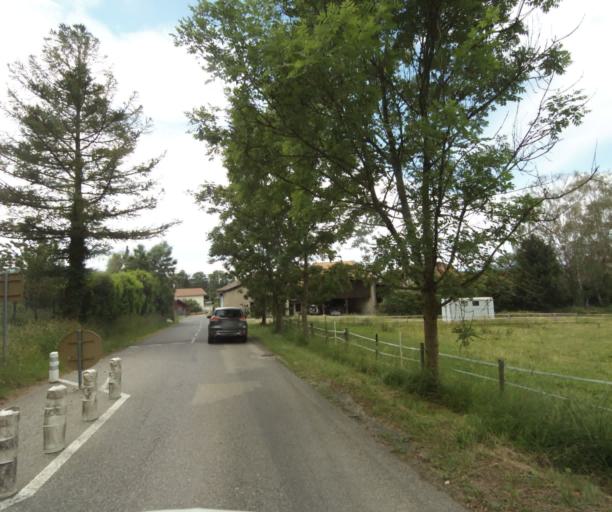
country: FR
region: Rhone-Alpes
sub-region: Departement de la Haute-Savoie
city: Bons-en-Chablais
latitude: 46.2663
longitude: 6.3877
